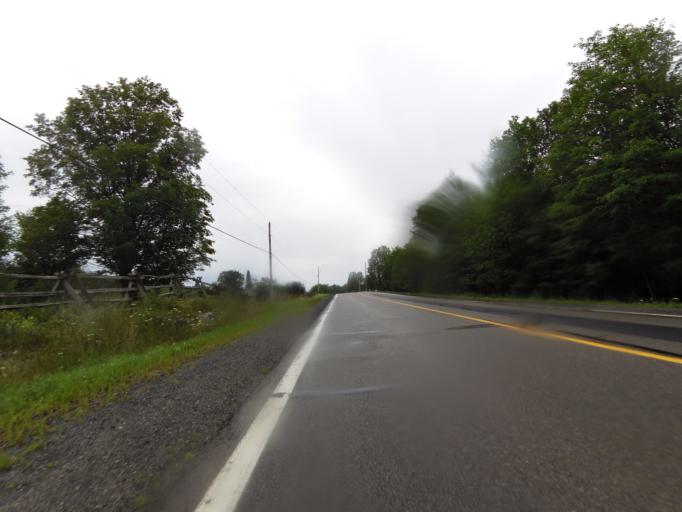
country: CA
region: Ontario
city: Perth
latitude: 44.9899
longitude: -76.3929
